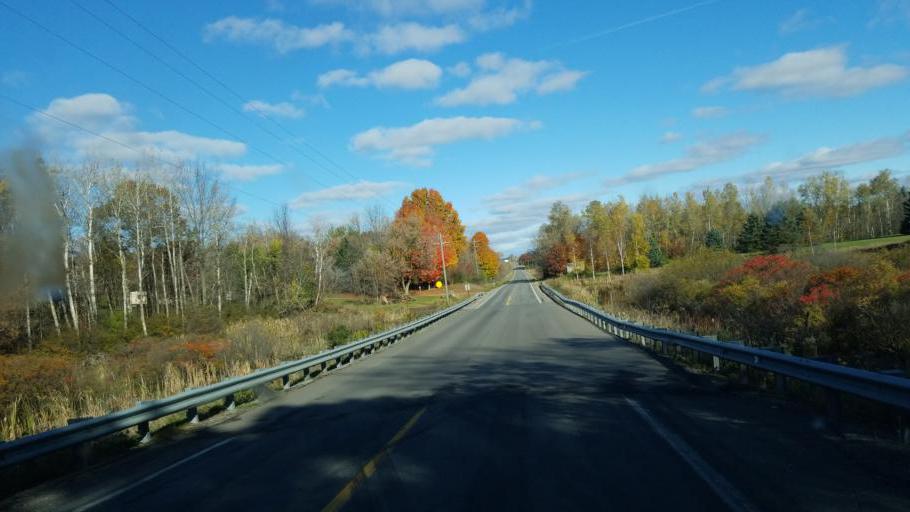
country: US
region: Michigan
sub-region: Montcalm County
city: Edmore
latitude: 43.4402
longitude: -85.0442
